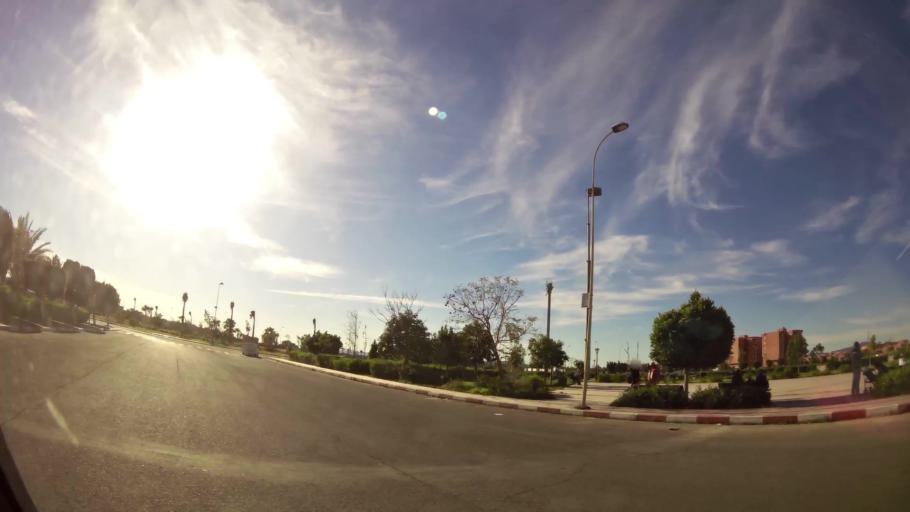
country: MA
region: Marrakech-Tensift-Al Haouz
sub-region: Marrakech
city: Marrakesh
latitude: 31.7542
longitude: -8.1098
